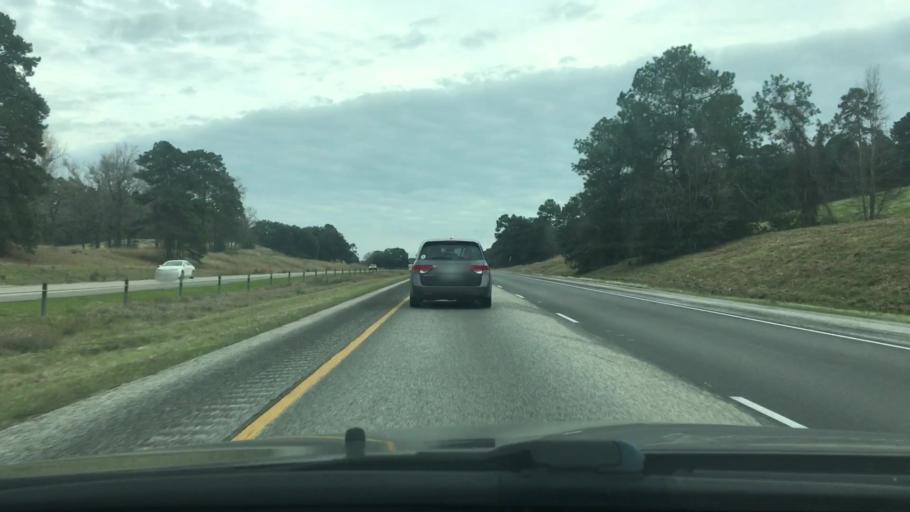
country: US
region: Texas
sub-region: Walker County
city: Huntsville
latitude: 30.8178
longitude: -95.7003
